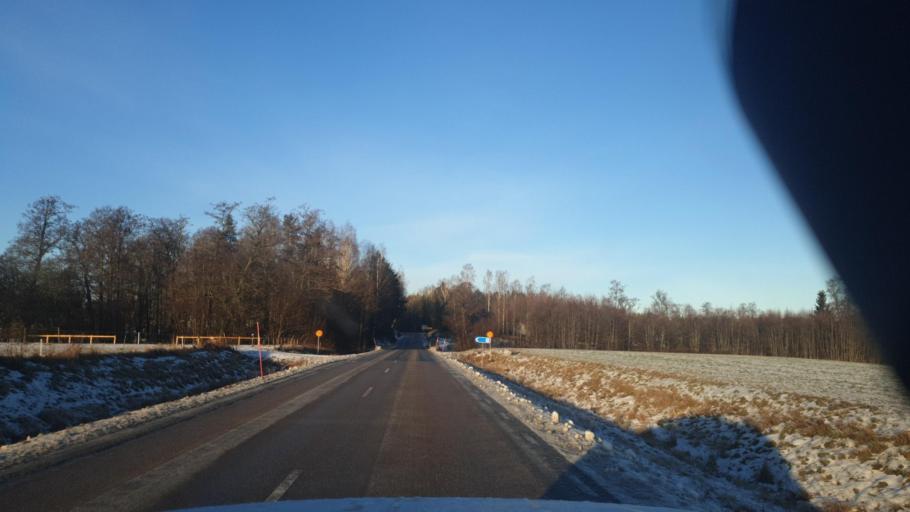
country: SE
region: Vaermland
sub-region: Arvika Kommun
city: Arvika
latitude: 59.5269
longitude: 12.6181
